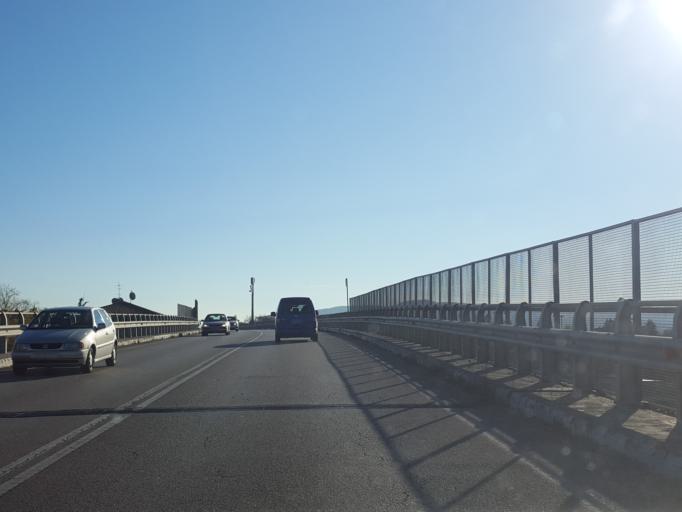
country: IT
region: Veneto
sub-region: Provincia di Vicenza
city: Villaggio Montegrappa
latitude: 45.5409
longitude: 11.5867
